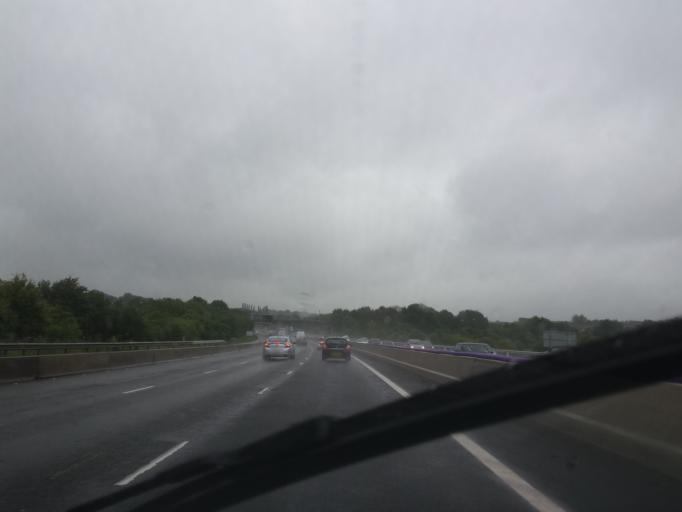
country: GB
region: England
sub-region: Derbyshire
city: Blackwell
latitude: 53.1149
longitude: -1.3335
